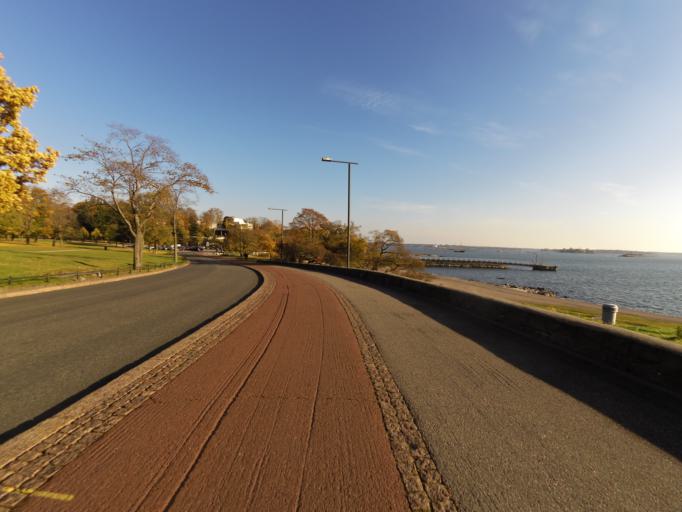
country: FI
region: Uusimaa
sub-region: Helsinki
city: Helsinki
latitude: 60.1539
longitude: 24.9576
